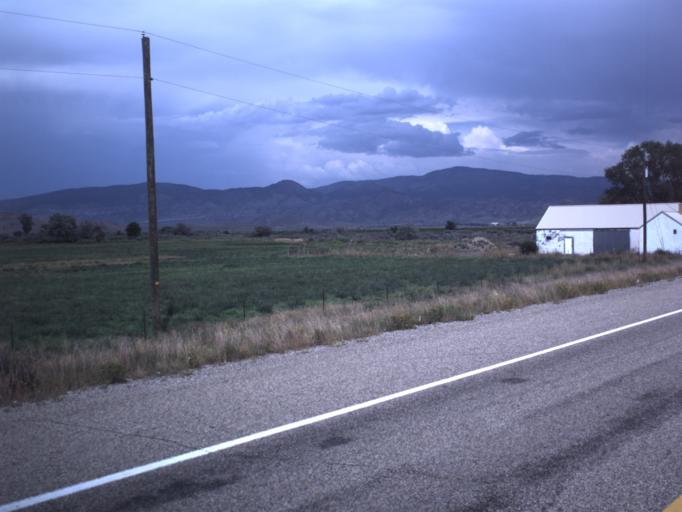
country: US
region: Utah
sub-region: Piute County
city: Junction
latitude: 38.1718
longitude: -112.2650
